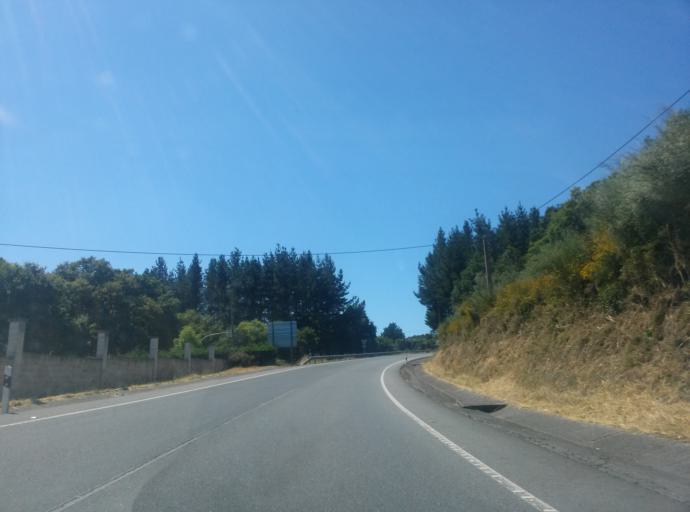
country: ES
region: Galicia
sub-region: Provincia de Lugo
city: Mos
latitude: 43.0985
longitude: -7.4774
